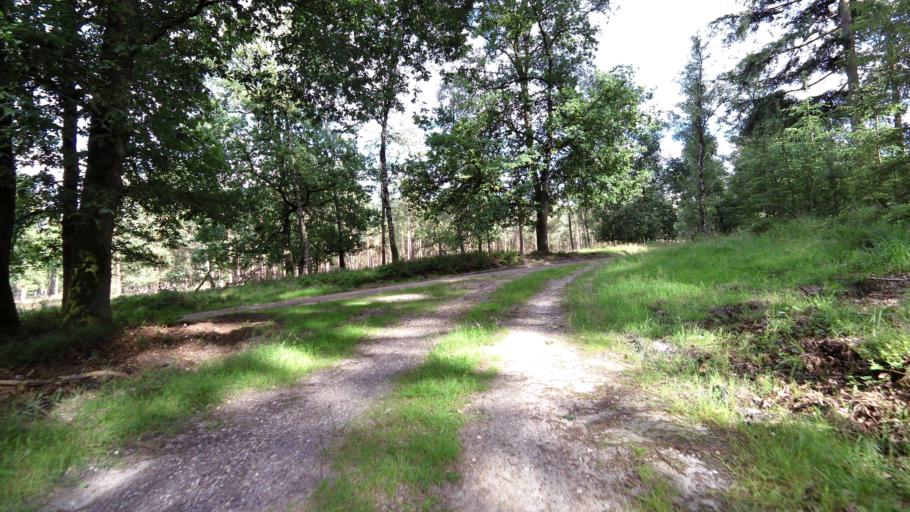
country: NL
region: Gelderland
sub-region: Gemeente Apeldoorn
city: Uddel
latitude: 52.2819
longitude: 5.8665
